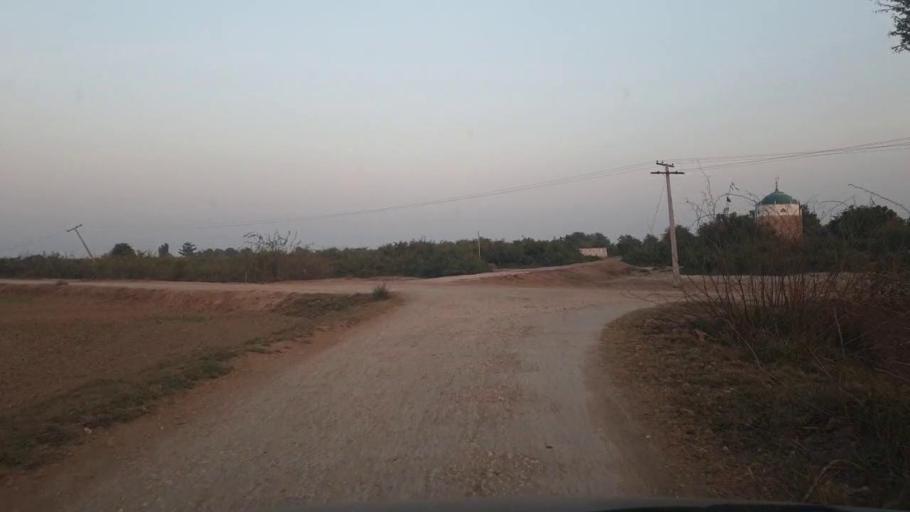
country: PK
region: Sindh
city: Bhit Shah
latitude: 25.8439
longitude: 68.5282
